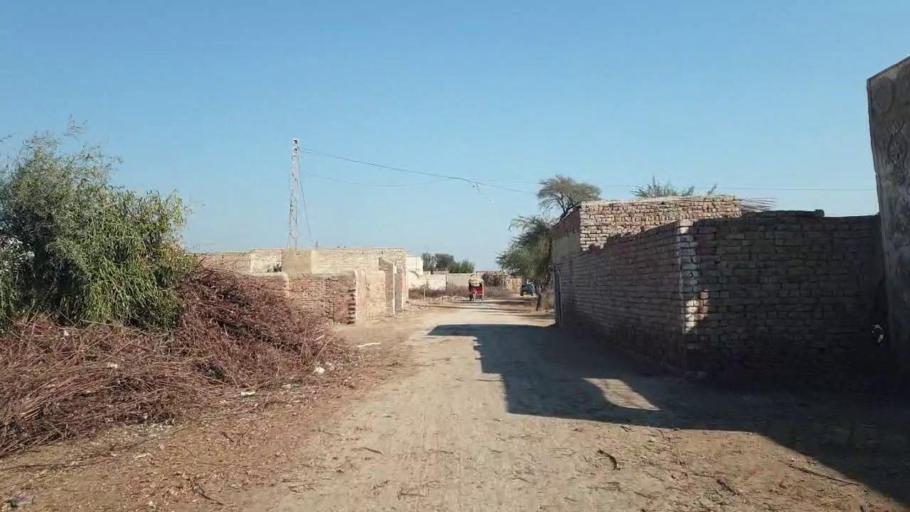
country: PK
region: Sindh
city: Shahdadpur
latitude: 25.9782
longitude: 68.6670
